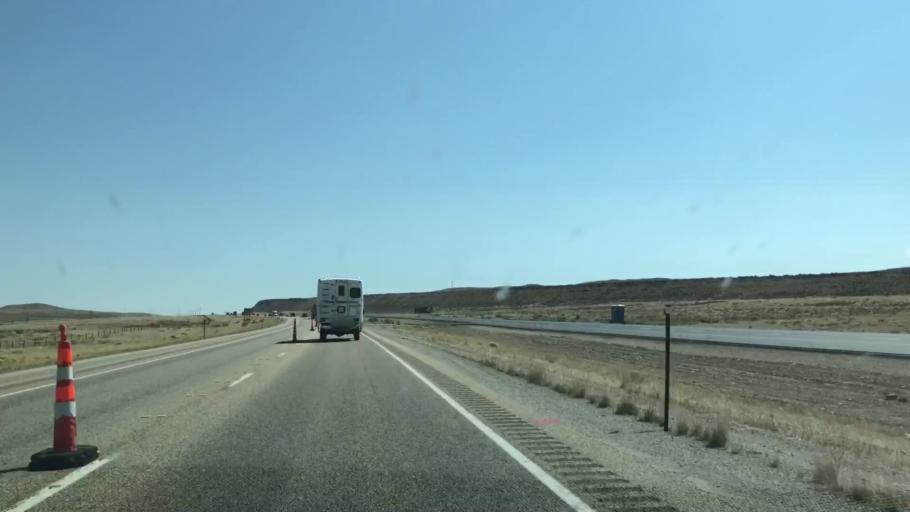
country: US
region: Wyoming
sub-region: Carbon County
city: Saratoga
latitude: 41.7456
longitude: -106.9272
